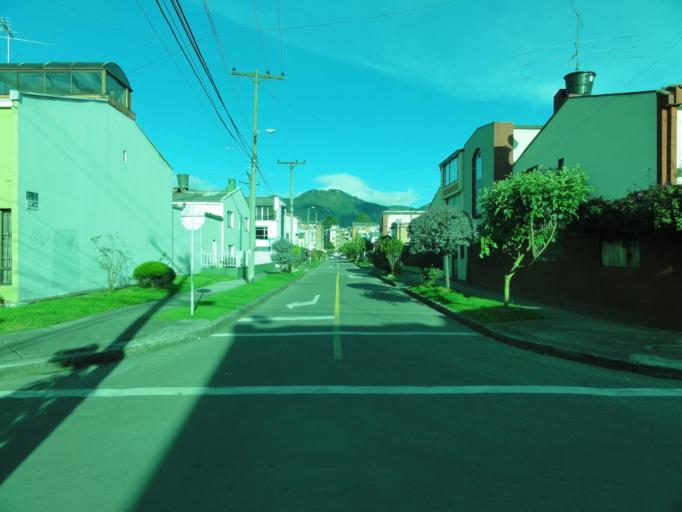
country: CO
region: Bogota D.C.
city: Bogota
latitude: 4.6537
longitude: -74.0861
